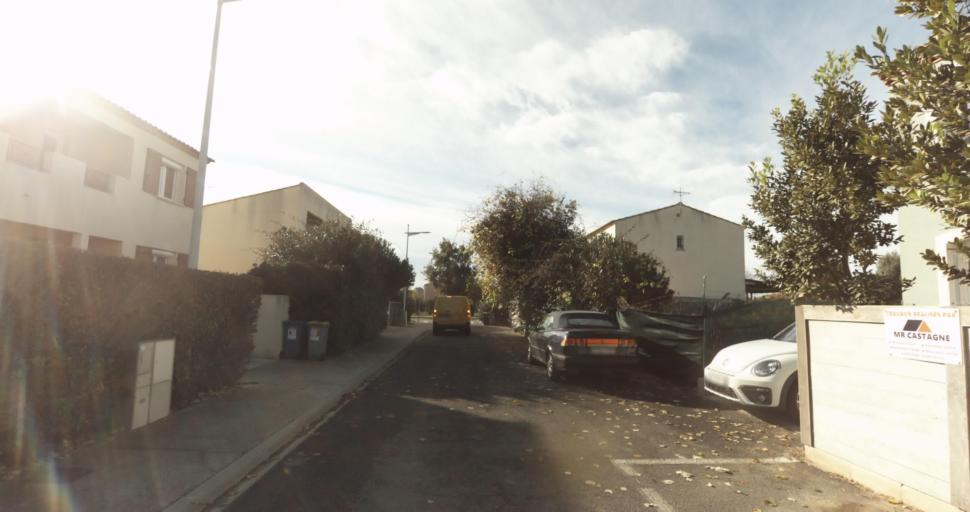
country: FR
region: Languedoc-Roussillon
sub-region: Departement du Gard
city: Aigues-Mortes
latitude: 43.5736
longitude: 4.1831
